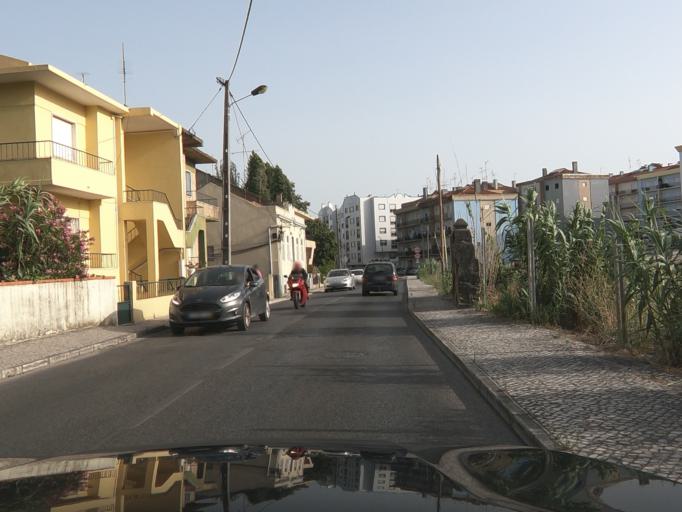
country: PT
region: Setubal
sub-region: Setubal
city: Setubal
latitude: 38.5364
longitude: -8.8983
